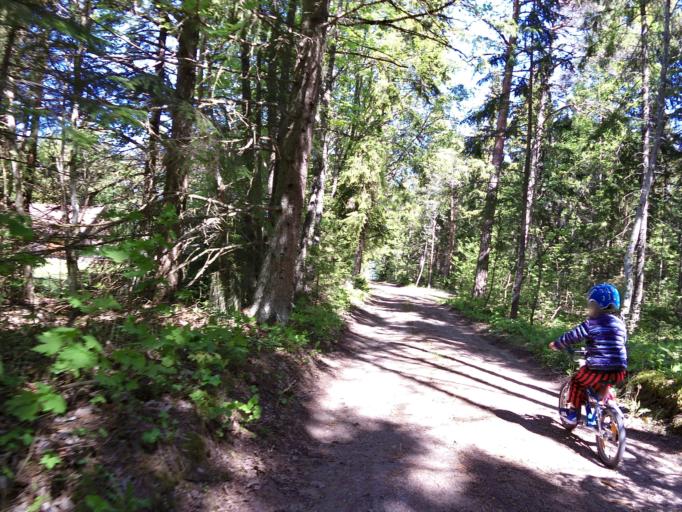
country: EE
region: Harju
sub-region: Paldiski linn
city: Paldiski
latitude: 59.2686
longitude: 23.7612
